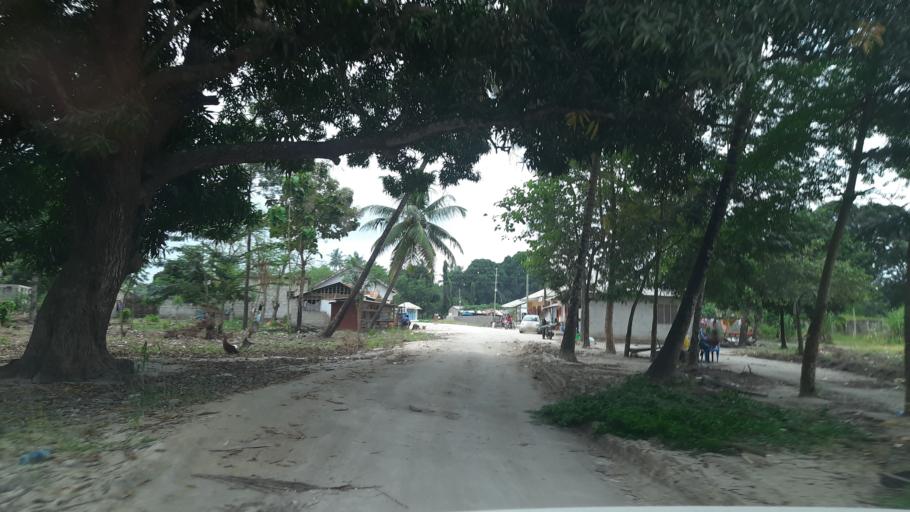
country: TZ
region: Pwani
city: Bagamoyo
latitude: -6.5103
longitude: 38.9316
